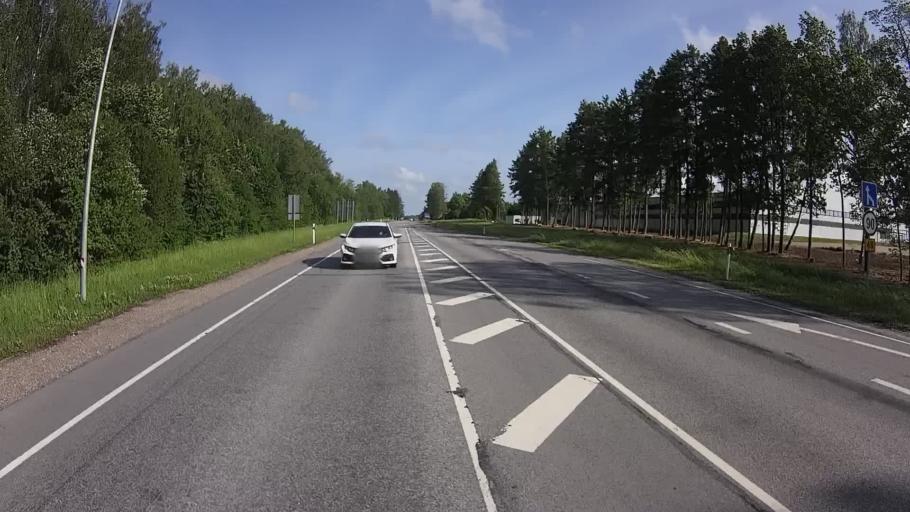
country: EE
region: Viljandimaa
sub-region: Viljandi linn
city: Viljandi
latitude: 58.3411
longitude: 25.5677
